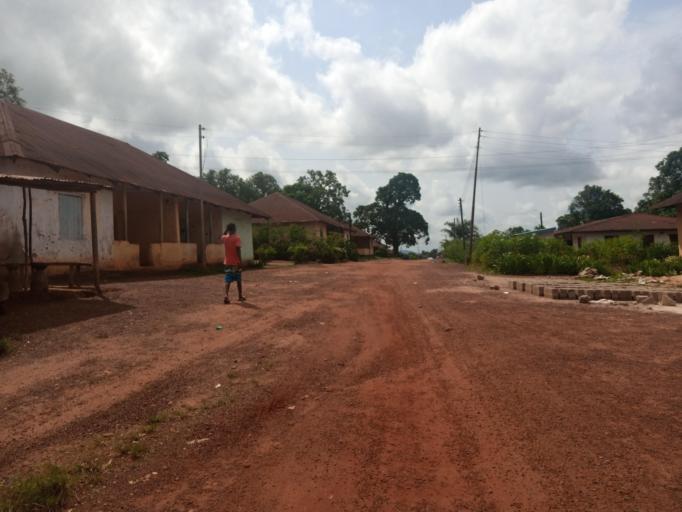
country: SL
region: Southern Province
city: Bo
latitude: 7.9713
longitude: -11.7417
